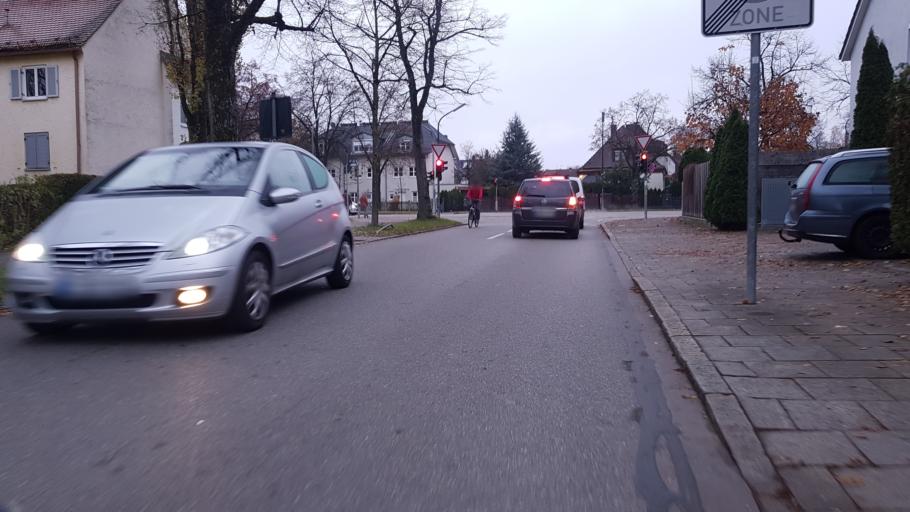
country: DE
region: Bavaria
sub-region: Upper Bavaria
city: Bogenhausen
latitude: 48.1175
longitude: 11.6247
